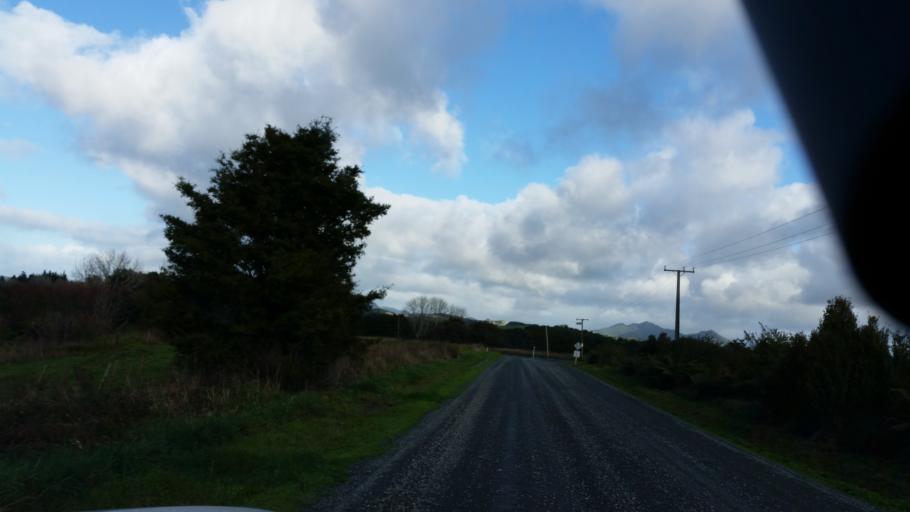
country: NZ
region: Northland
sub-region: Whangarei
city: Maungatapere
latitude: -35.7191
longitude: 174.0709
